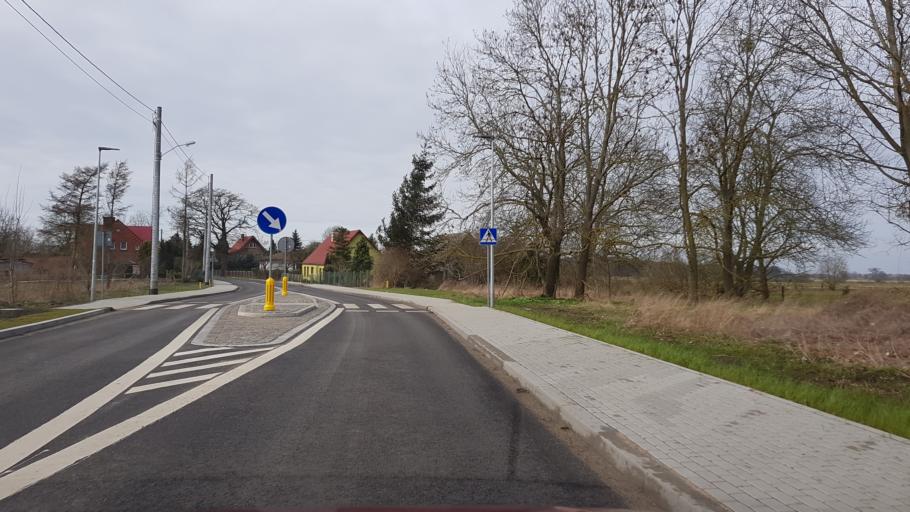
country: PL
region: West Pomeranian Voivodeship
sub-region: Powiat policki
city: Nowe Warpno
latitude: 53.6947
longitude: 14.3621
